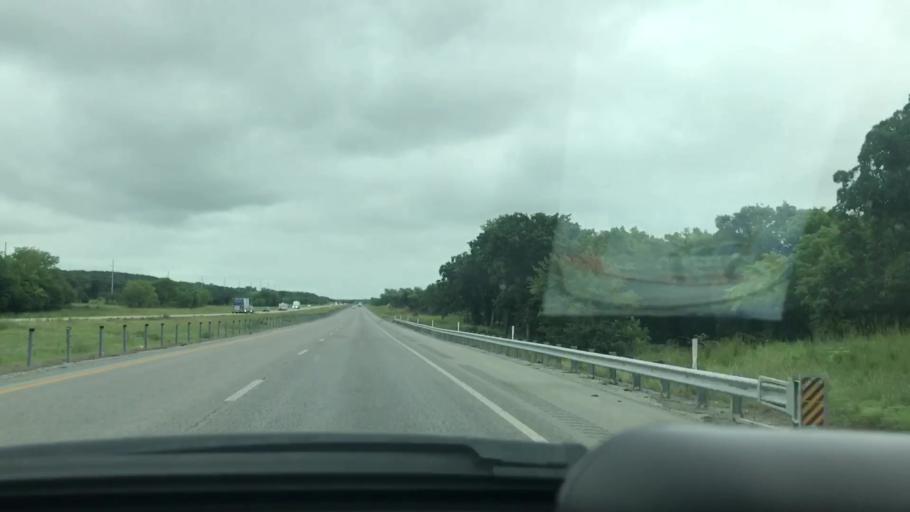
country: US
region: Oklahoma
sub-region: Coal County
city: Coalgate
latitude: 34.6307
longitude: -95.9569
